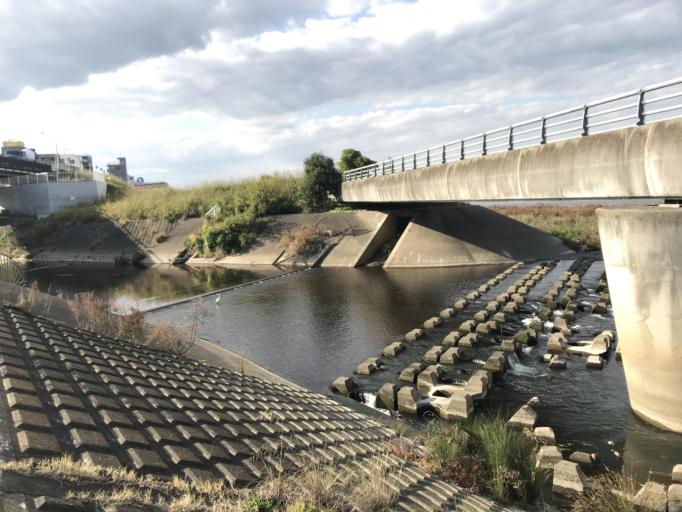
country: JP
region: Tokyo
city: Chofugaoka
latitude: 35.6084
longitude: 139.6202
